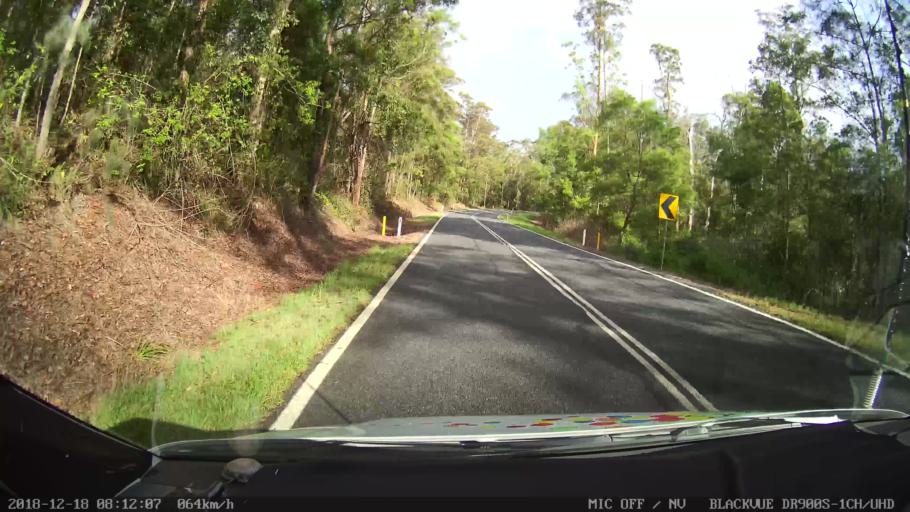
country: AU
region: New South Wales
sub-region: Kyogle
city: Kyogle
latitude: -28.3425
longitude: 152.6702
